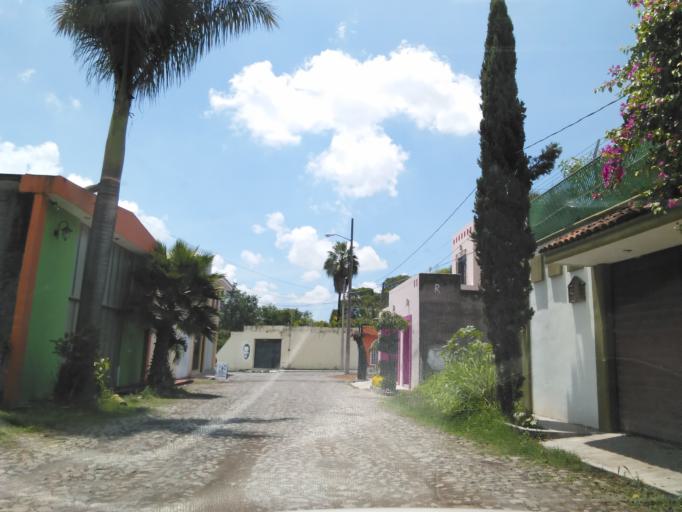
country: MX
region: Nayarit
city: Tepic
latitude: 21.5136
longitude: -104.9135
